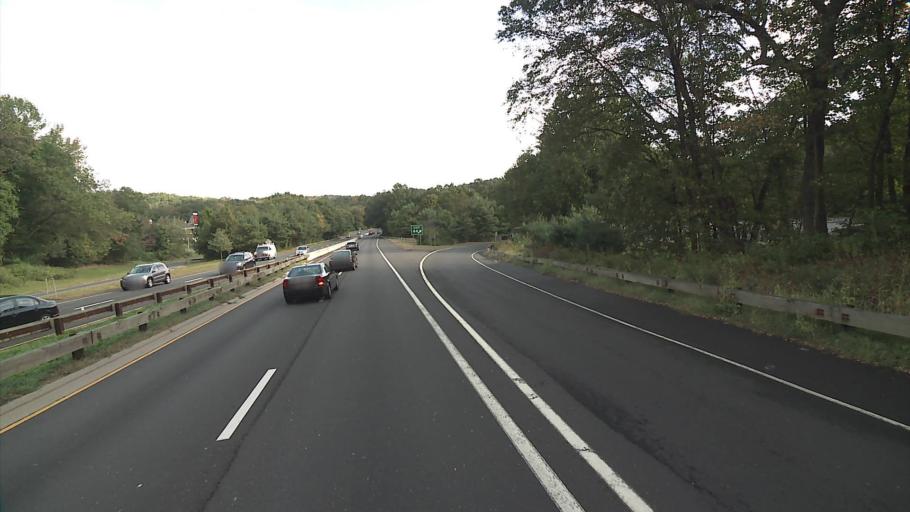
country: US
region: Connecticut
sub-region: Fairfield County
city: Fairfield
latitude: 41.2012
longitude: -73.2716
